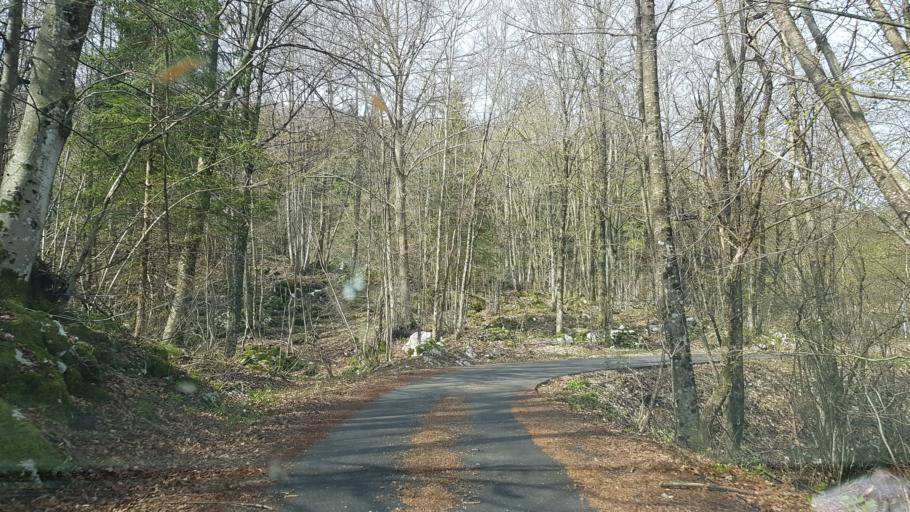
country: IT
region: Friuli Venezia Giulia
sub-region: Provincia di Udine
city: Trasaghis
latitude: 46.2863
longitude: 13.0163
